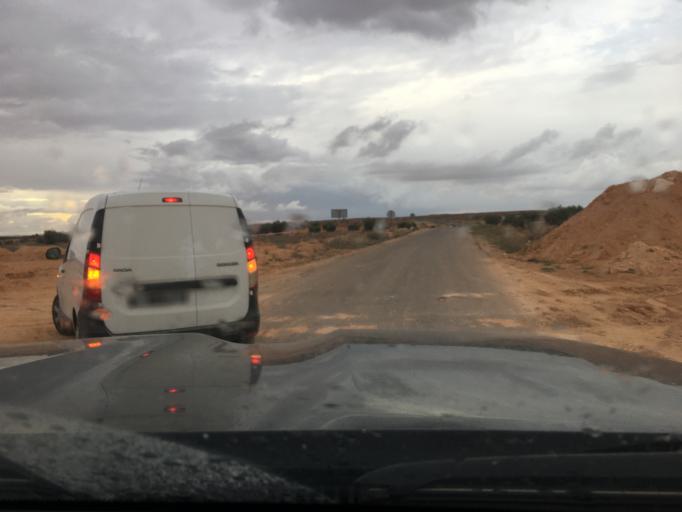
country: TN
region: Madanin
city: Medenine
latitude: 33.3188
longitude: 10.6051
